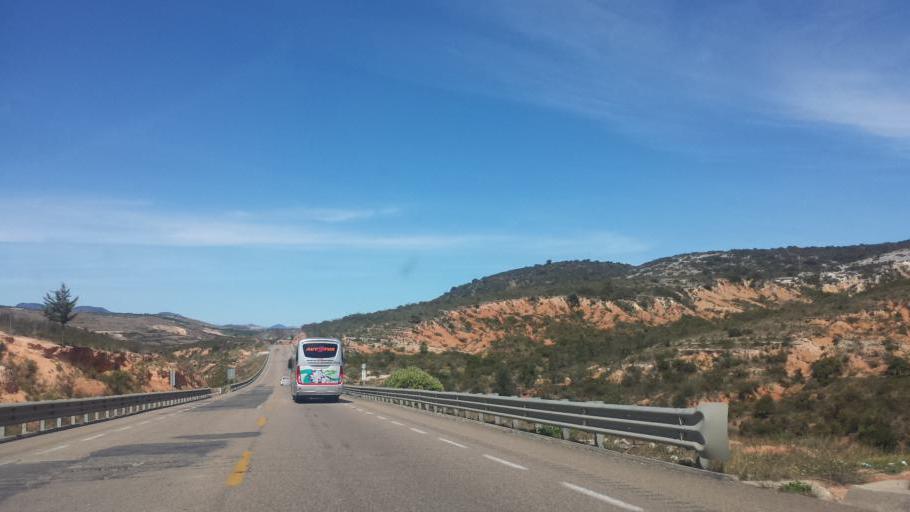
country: MX
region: Oaxaca
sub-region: Villa Tejupam de la Union
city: Villa Tejupam de la Union
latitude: 17.6824
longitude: -97.3563
